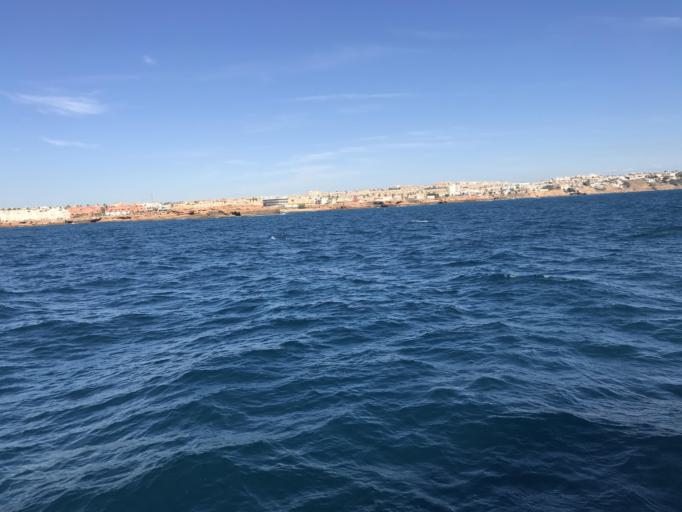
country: ES
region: Valencia
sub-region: Provincia de Alicante
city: Torrevieja
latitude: 37.9824
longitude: -0.6516
